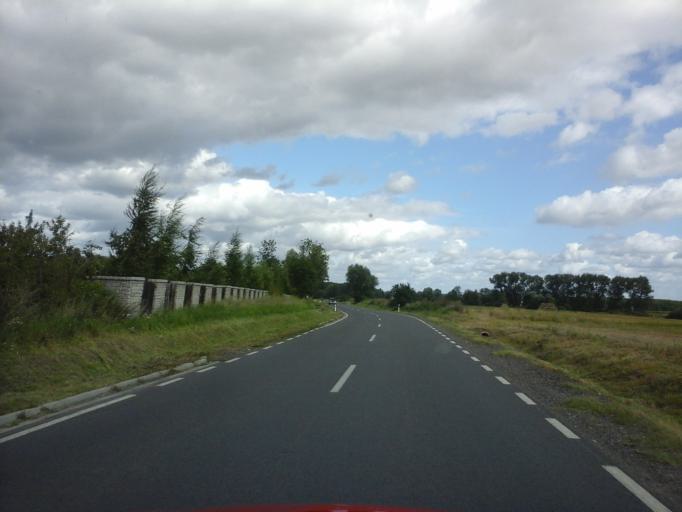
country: PL
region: West Pomeranian Voivodeship
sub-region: Powiat stargardzki
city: Kobylanka
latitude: 53.3374
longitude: 14.9423
